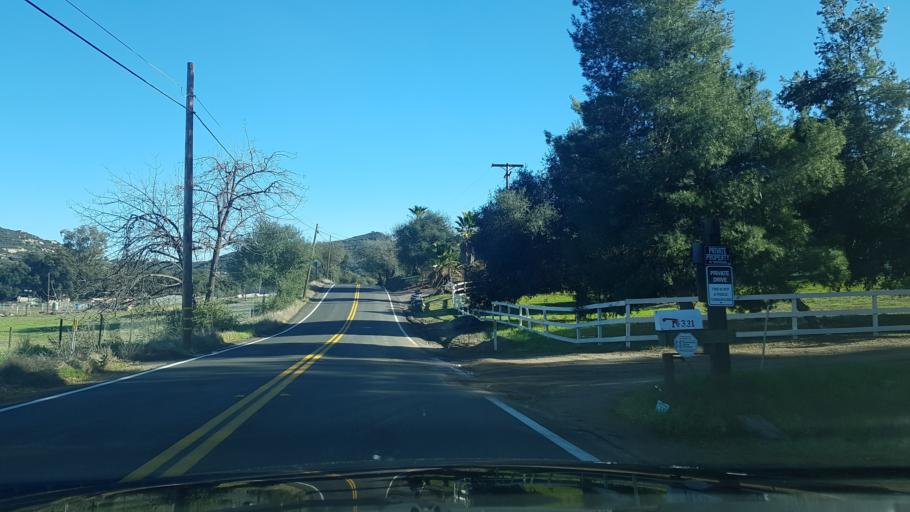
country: US
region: California
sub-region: San Diego County
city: Valley Center
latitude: 33.2041
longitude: -116.9748
